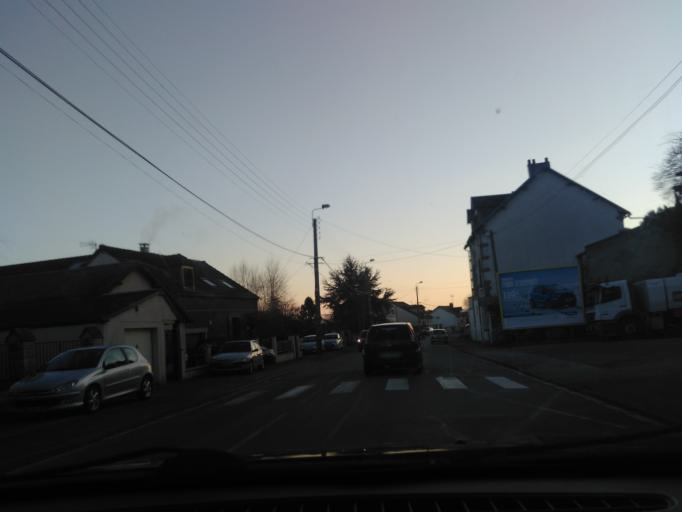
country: FR
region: Picardie
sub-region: Departement de l'Aisne
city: Laon
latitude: 49.5610
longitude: 3.6319
